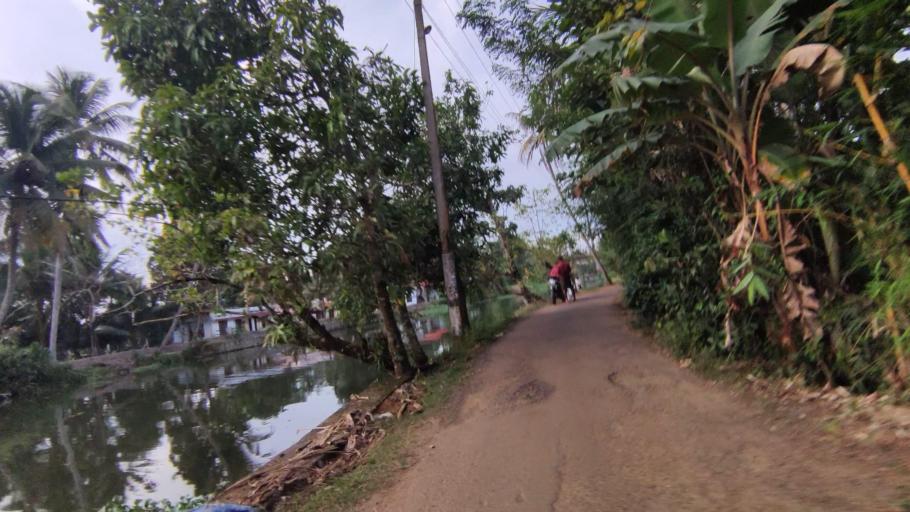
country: IN
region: Kerala
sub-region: Kottayam
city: Kottayam
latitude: 9.6461
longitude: 76.4787
